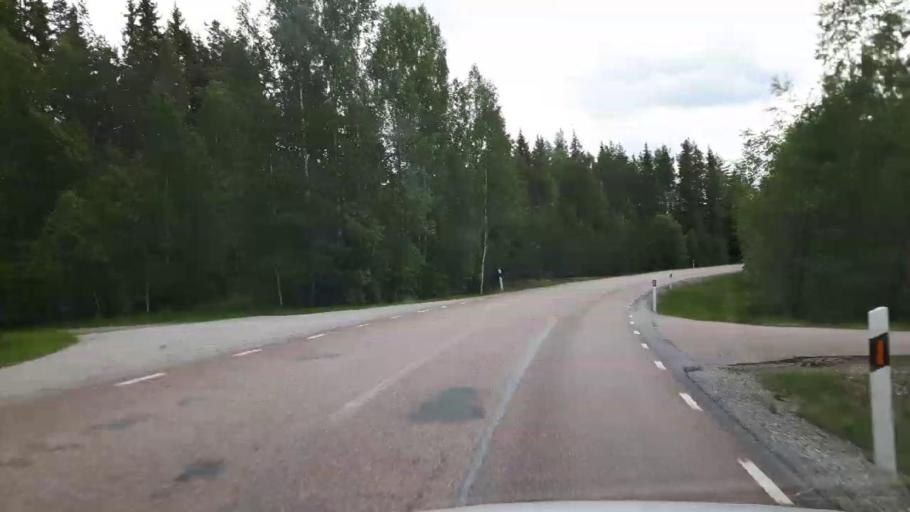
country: SE
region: Vaestmanland
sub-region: Fagersta Kommun
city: Fagersta
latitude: 59.8826
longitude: 15.8360
